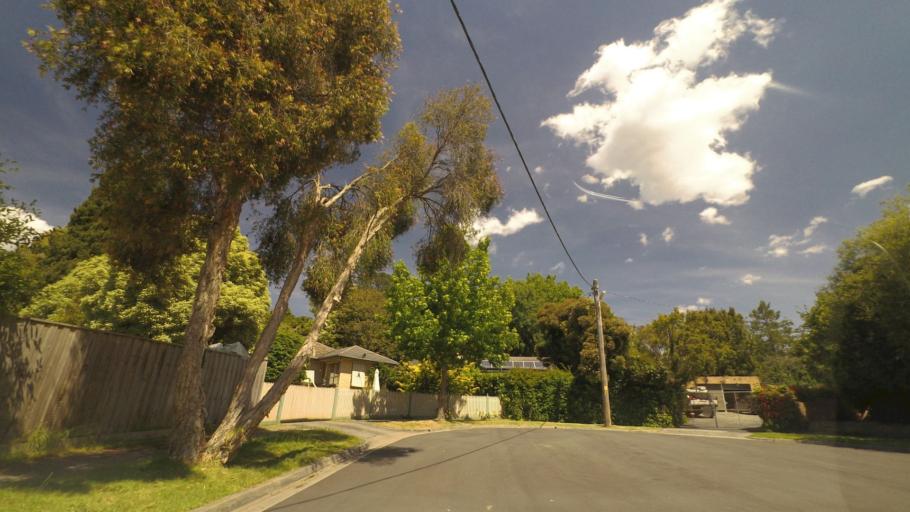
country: AU
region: Victoria
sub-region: Yarra Ranges
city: Montrose
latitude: -37.8073
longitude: 145.3412
